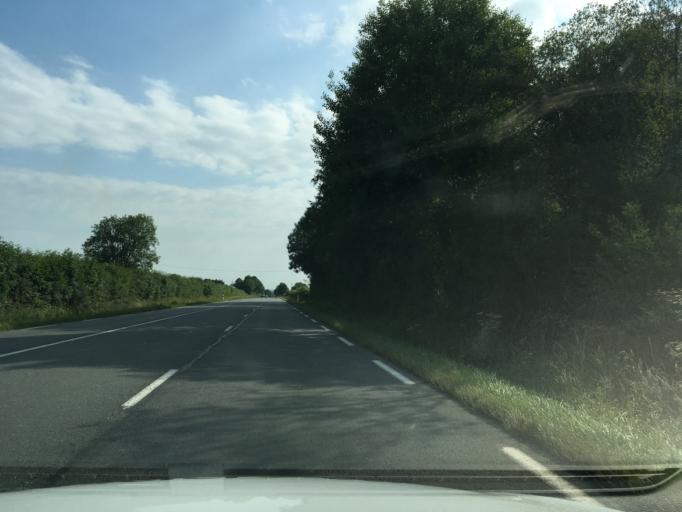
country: FR
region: Poitou-Charentes
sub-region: Departement des Deux-Sevres
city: Champdeniers-Saint-Denis
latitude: 46.5013
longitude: -0.3394
